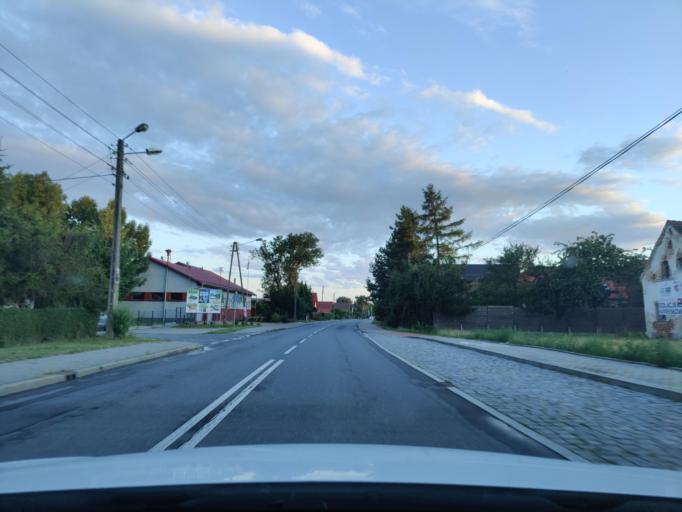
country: PL
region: Opole Voivodeship
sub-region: Powiat nyski
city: Chroscina
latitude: 50.6549
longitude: 17.3879
